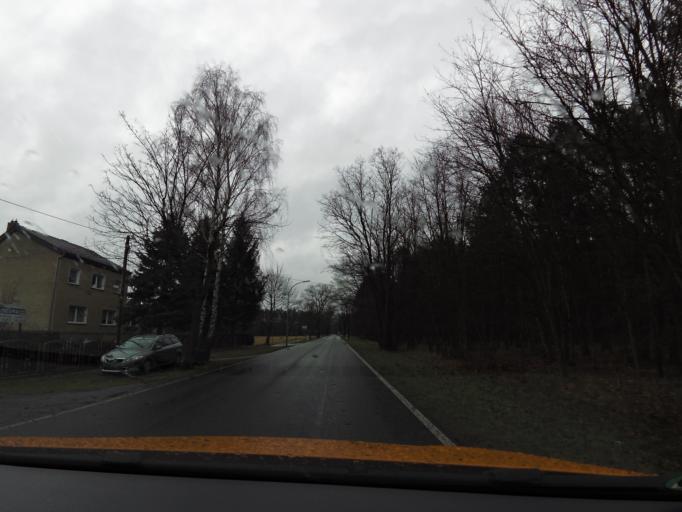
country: DE
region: Brandenburg
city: Am Mellensee
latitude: 52.1698
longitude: 13.3770
